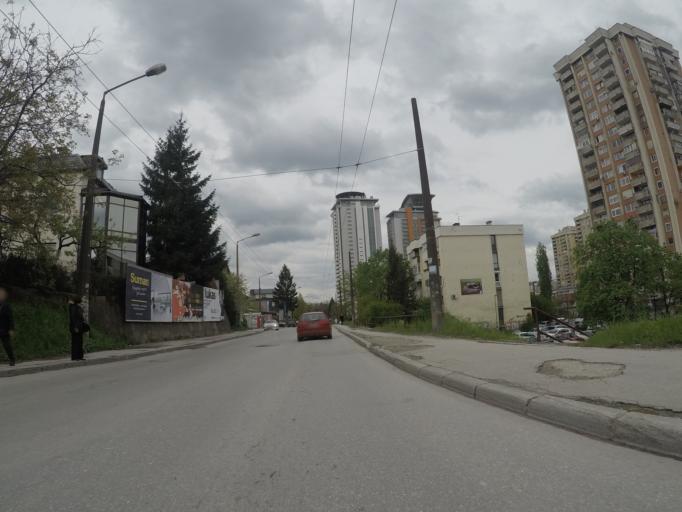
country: BA
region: Federation of Bosnia and Herzegovina
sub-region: Kanton Sarajevo
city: Sarajevo
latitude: 43.8464
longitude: 18.3787
